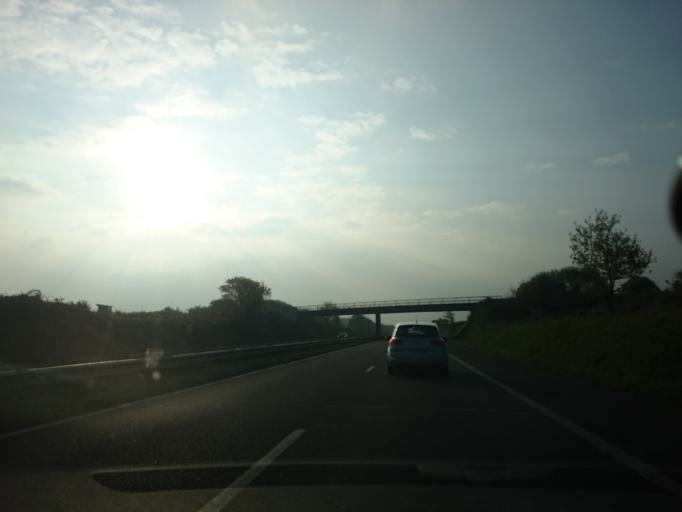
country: FR
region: Brittany
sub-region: Departement du Finistere
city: Le Trevoux
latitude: 47.8813
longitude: -3.6748
